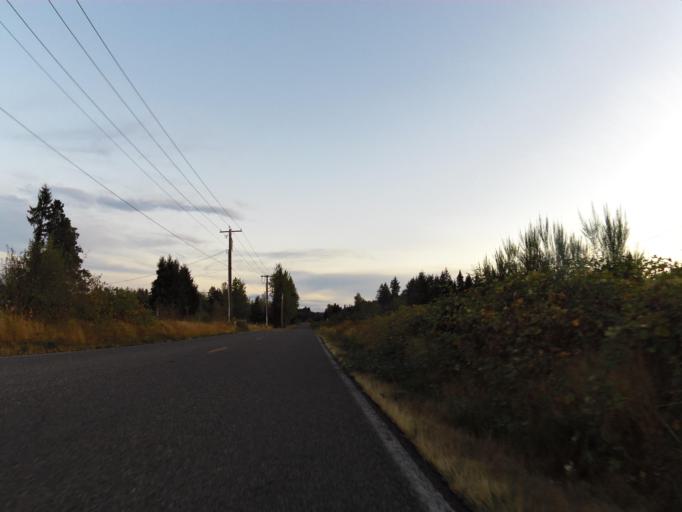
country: US
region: Washington
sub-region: Thurston County
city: Tenino
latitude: 46.8243
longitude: -122.8616
